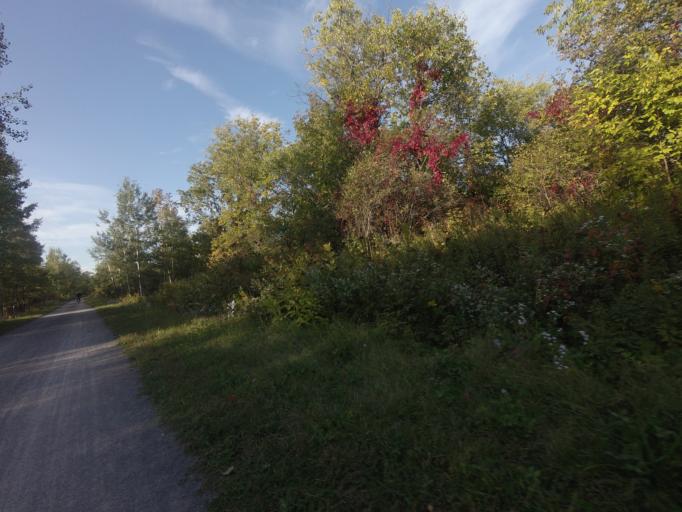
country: CA
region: Quebec
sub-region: Laurentides
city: Prevost
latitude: 45.8355
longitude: -74.0583
